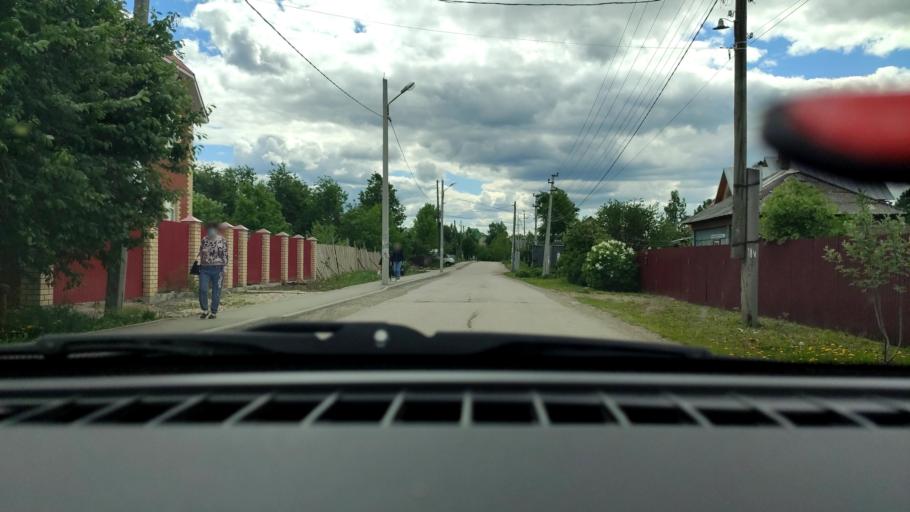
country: RU
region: Perm
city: Perm
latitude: 58.0455
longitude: 56.3591
